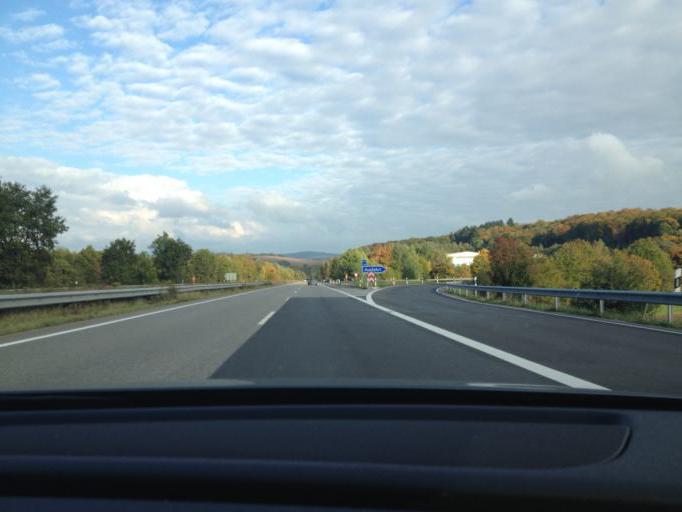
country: DE
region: Rheinland-Pfalz
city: Ehweiler
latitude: 49.5156
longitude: 7.3672
